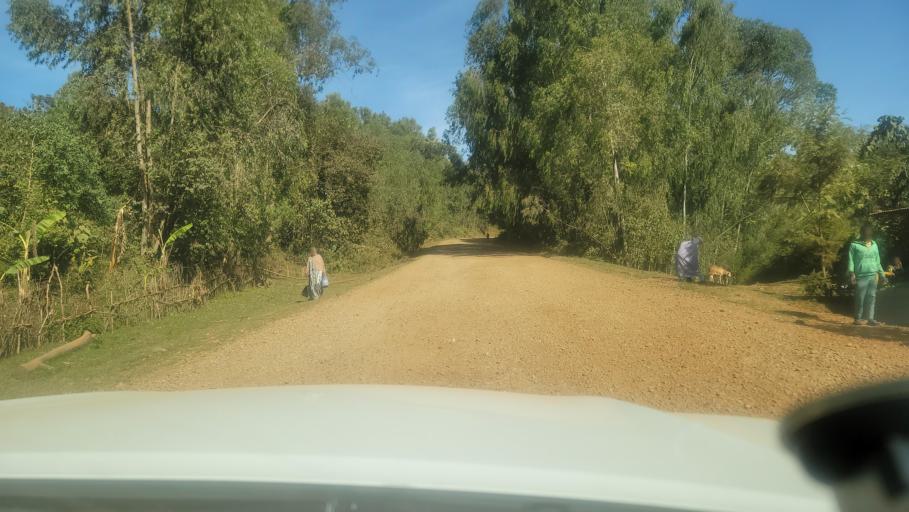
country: ET
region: Oromiya
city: Agaro
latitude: 7.8019
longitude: 36.4656
